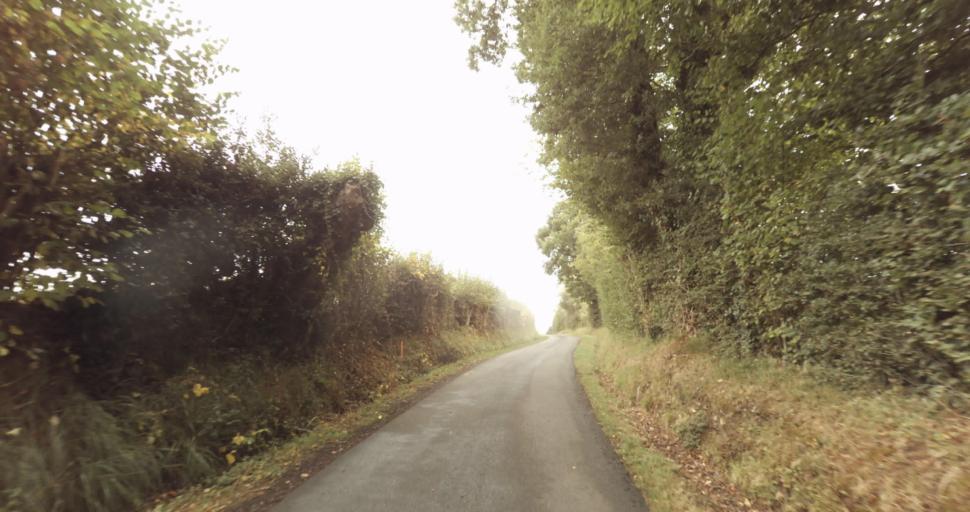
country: FR
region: Lower Normandy
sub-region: Departement de l'Orne
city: Gace
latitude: 48.8392
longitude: 0.3217
